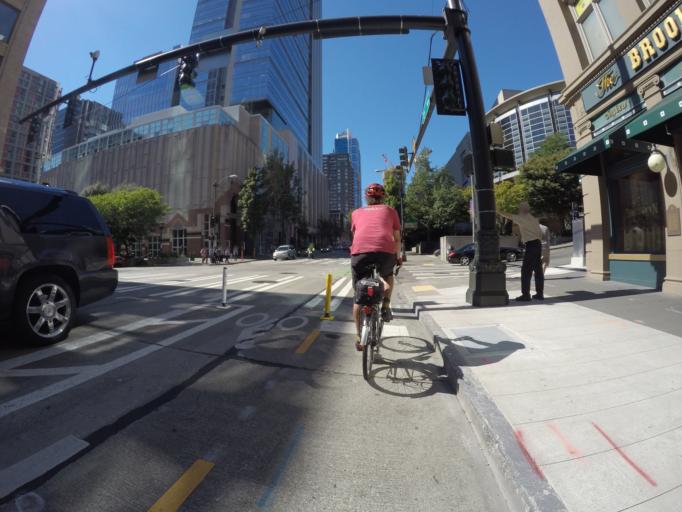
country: US
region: Washington
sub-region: King County
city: Seattle
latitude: 47.6068
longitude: -122.3365
